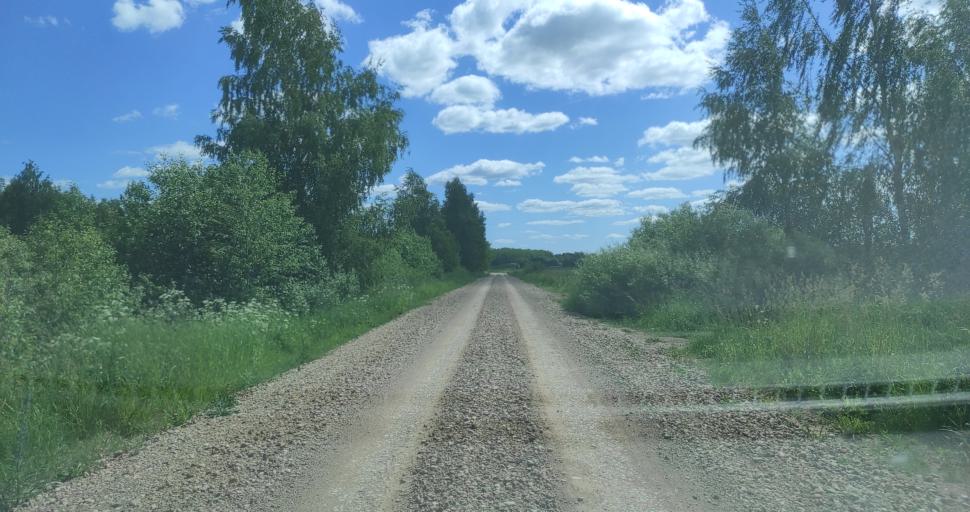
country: LV
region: Aizpute
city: Aizpute
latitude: 56.8470
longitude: 21.6914
